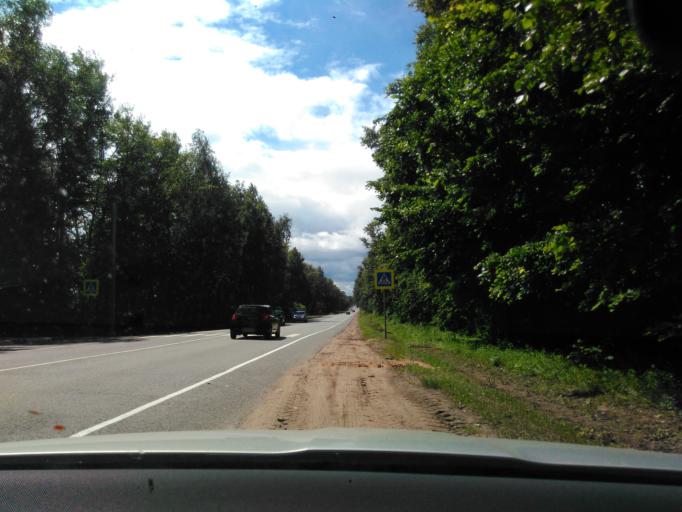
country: RU
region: Moskovskaya
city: Shevlyakovo
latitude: 56.3833
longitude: 36.8553
